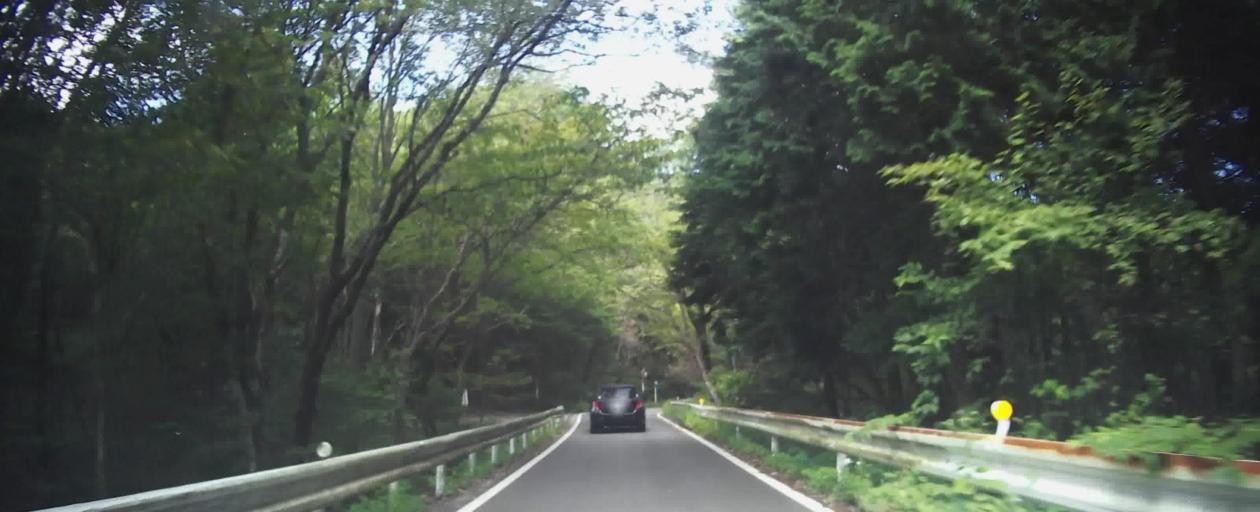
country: JP
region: Gunma
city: Shibukawa
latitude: 36.4652
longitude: 138.8890
